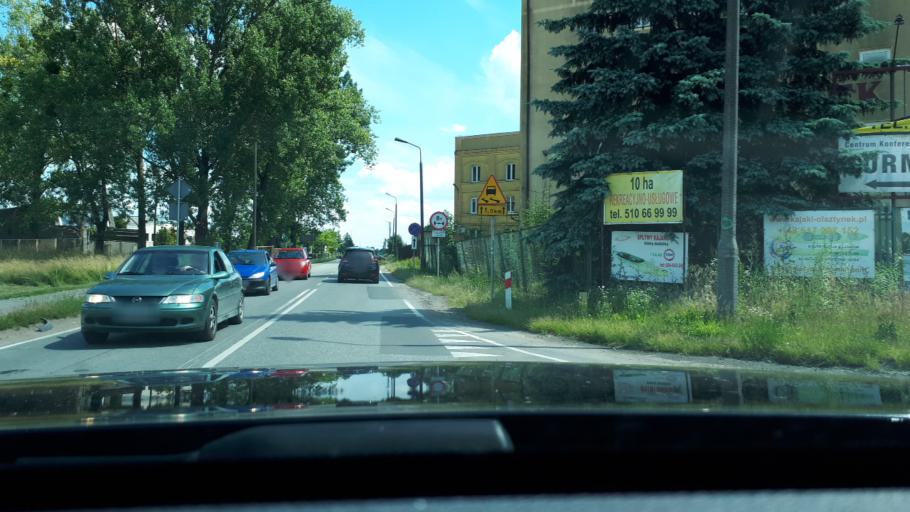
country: PL
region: Warmian-Masurian Voivodeship
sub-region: Powiat olsztynski
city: Olsztynek
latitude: 53.5816
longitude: 20.2933
